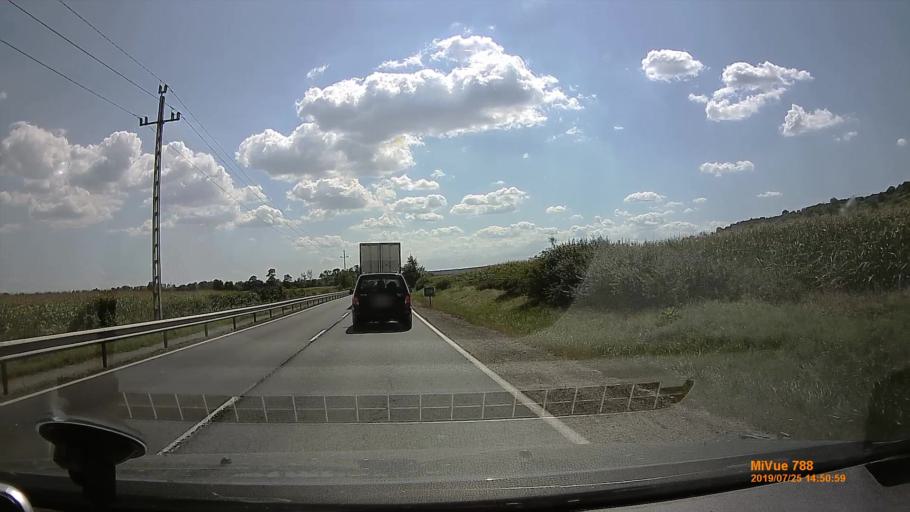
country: HU
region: Borsod-Abauj-Zemplen
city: Aszalo
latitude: 48.2184
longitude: 20.9474
